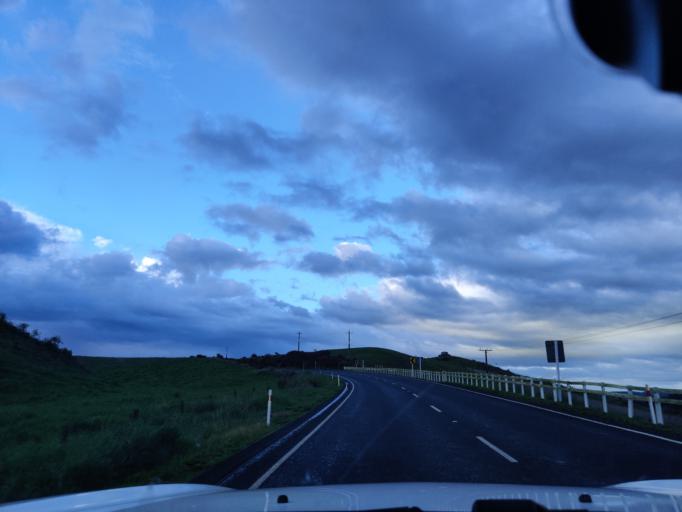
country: NZ
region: Waikato
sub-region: South Waikato District
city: Tokoroa
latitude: -38.3851
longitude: 175.7822
